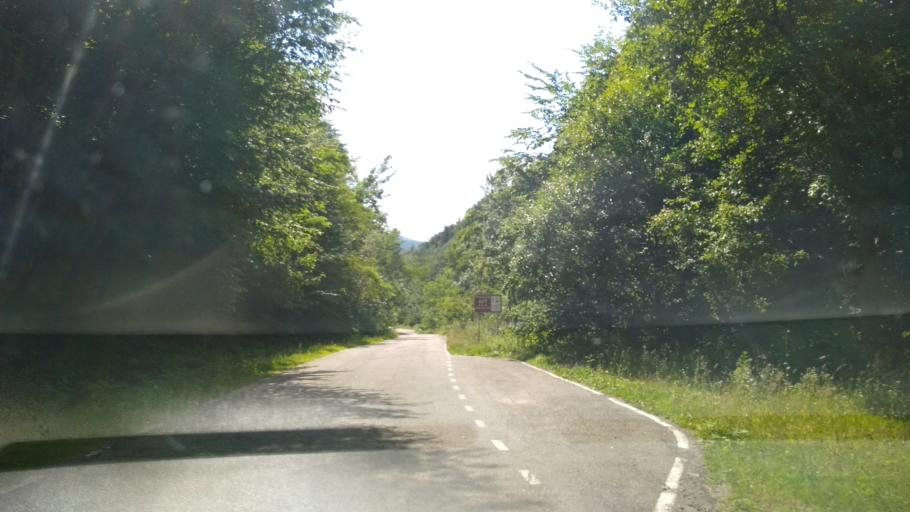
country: RO
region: Hunedoara
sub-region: Comuna Orastioara de Sus
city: Orastioara de Sus
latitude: 45.6222
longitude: 23.2976
